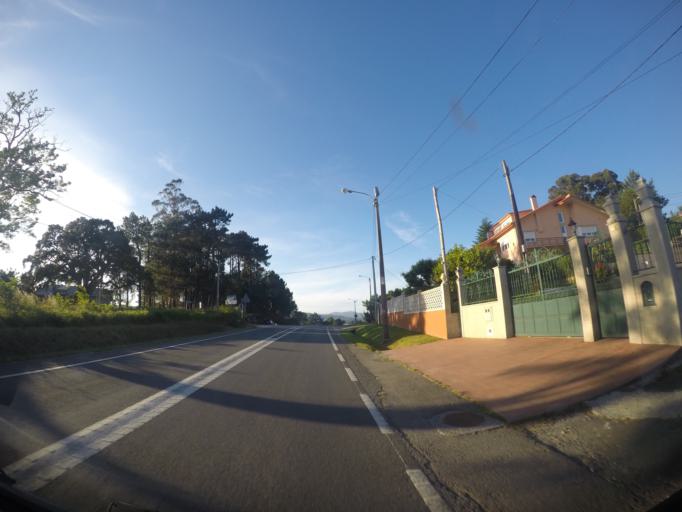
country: ES
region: Galicia
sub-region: Provincia da Coruna
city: Noia
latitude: 42.7716
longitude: -8.9365
